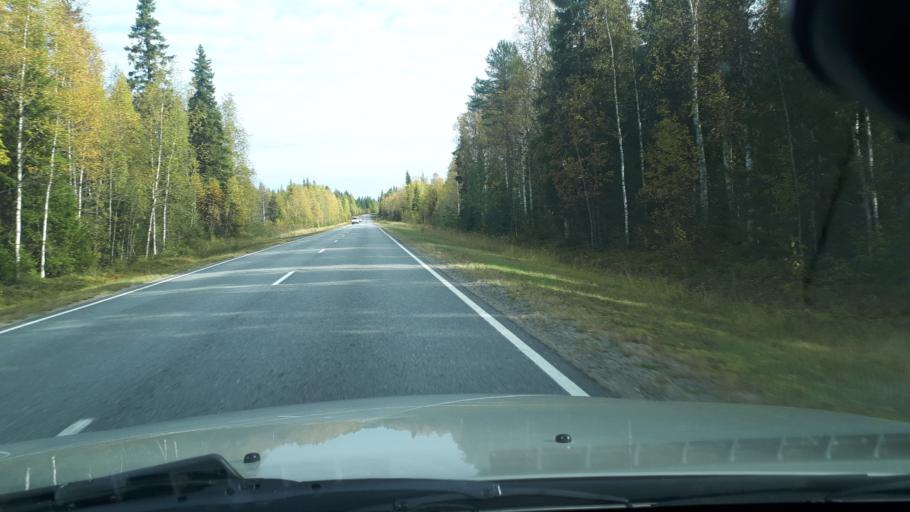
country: FI
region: Northern Ostrobothnia
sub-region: Oulu
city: Yli-Ii
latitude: 65.9464
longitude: 25.9009
